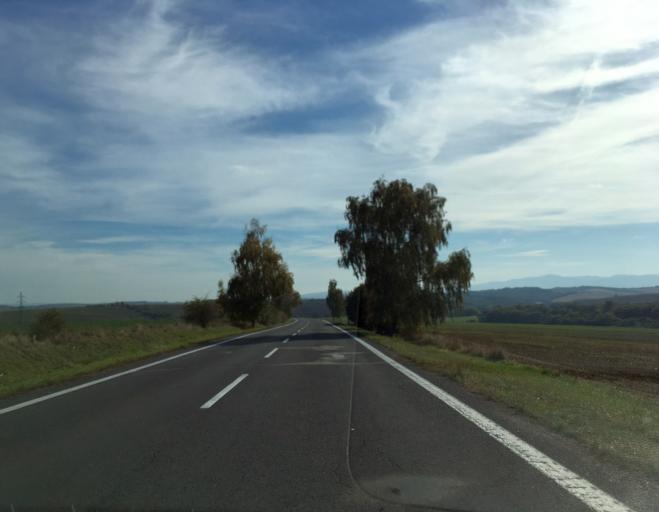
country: SK
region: Nitriansky
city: Zeliezovce
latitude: 48.1246
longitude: 18.7383
